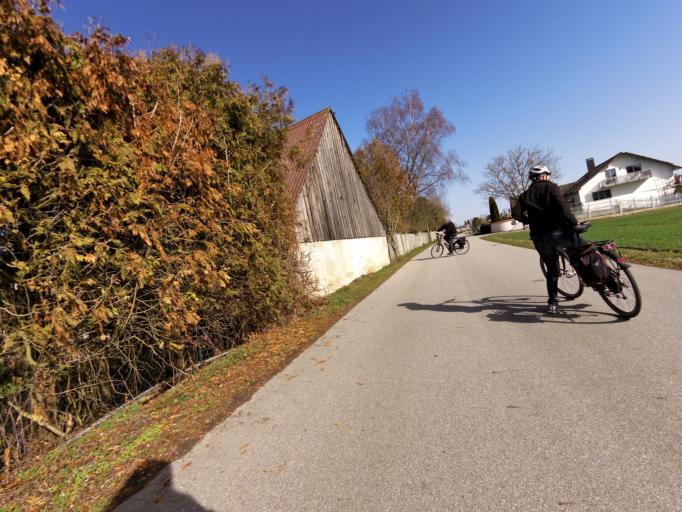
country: DE
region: Bavaria
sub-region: Lower Bavaria
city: Eching
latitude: 48.4997
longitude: 12.0461
